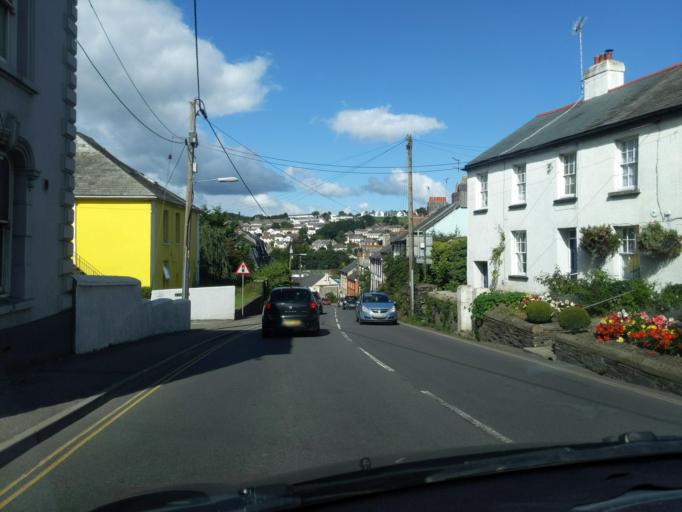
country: GB
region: England
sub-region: Cornwall
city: Launceston
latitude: 50.6392
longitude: -4.3643
